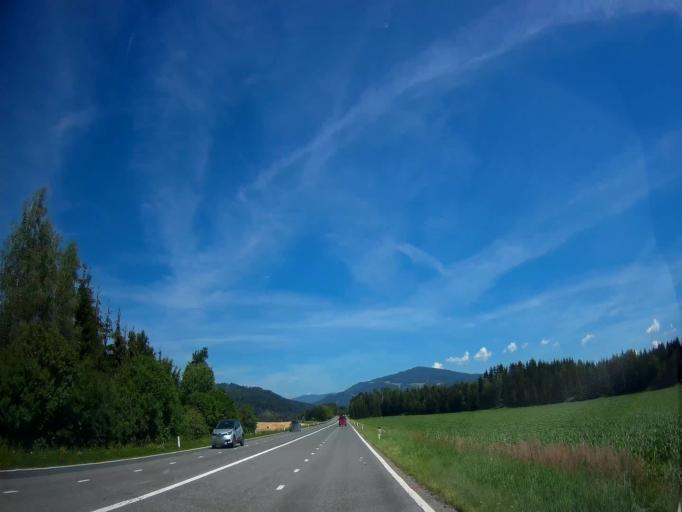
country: AT
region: Carinthia
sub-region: Politischer Bezirk Sankt Veit an der Glan
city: Molbling
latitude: 46.8482
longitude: 14.4482
